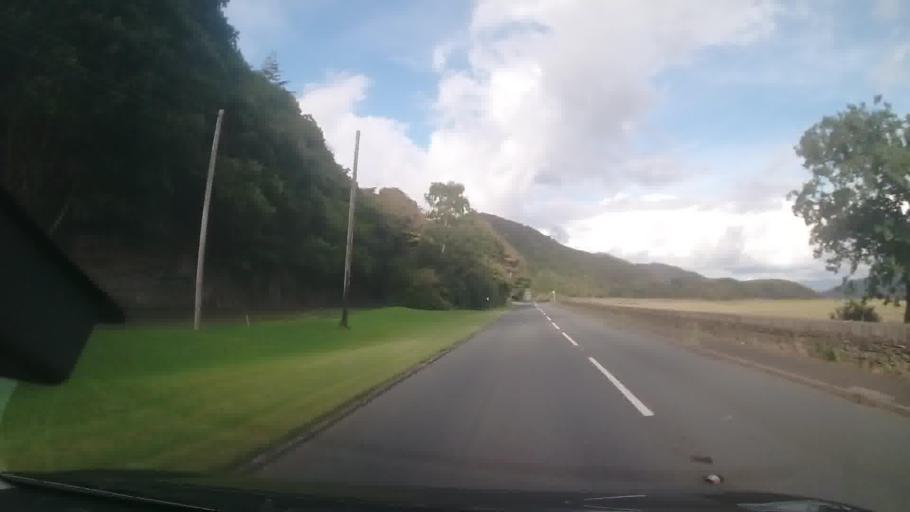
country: GB
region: Wales
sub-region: Gwynedd
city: Barmouth
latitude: 52.7333
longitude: -4.0283
